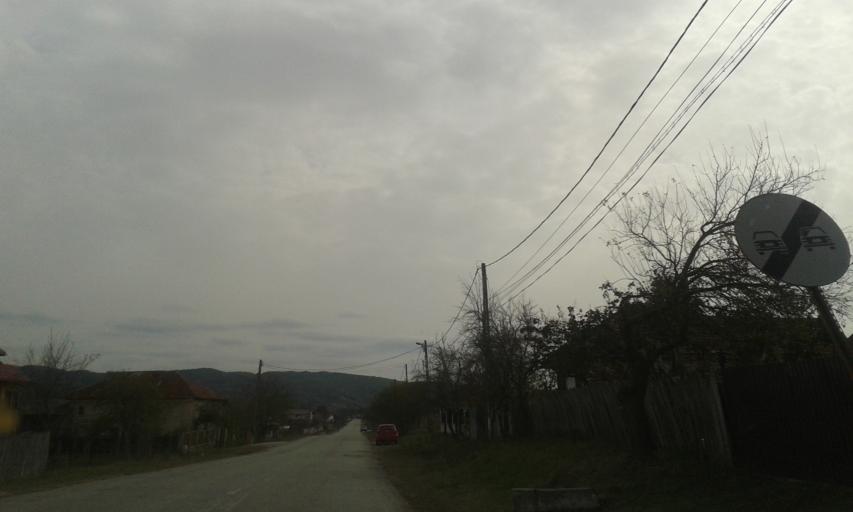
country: RO
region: Gorj
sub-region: Comuna Hurezani
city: Hurezani
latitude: 44.8233
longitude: 23.6484
